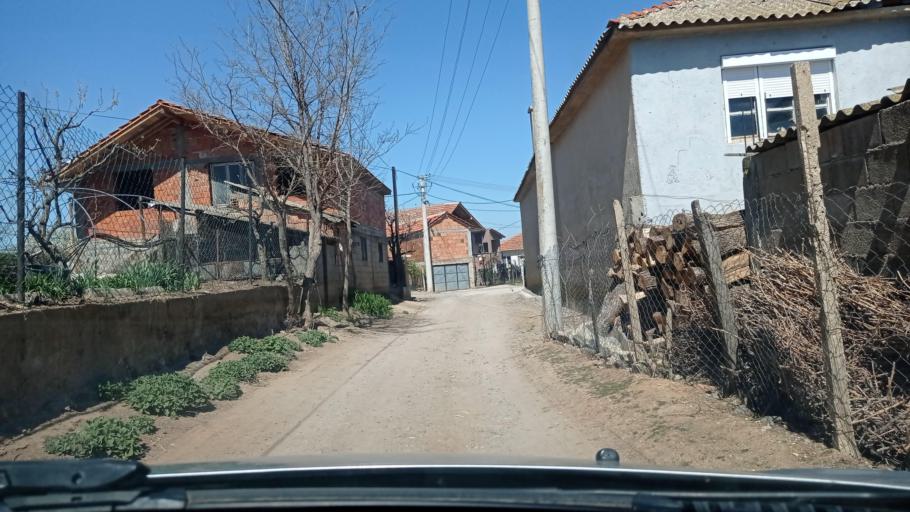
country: MK
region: Lozovo
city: Lozovo
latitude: 41.7633
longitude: 21.8650
